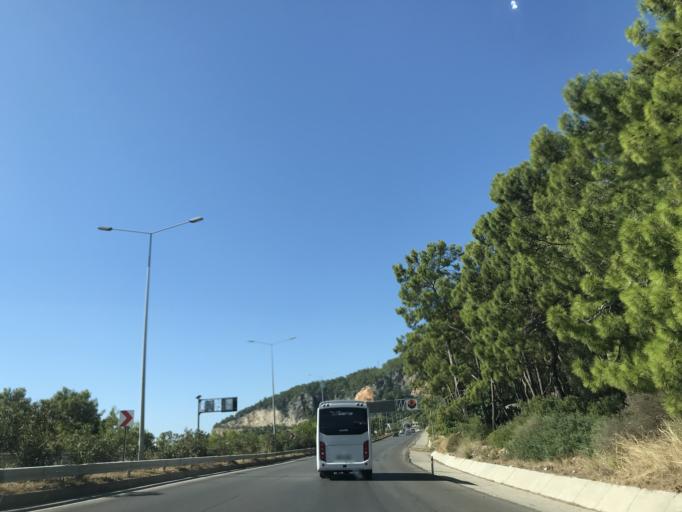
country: TR
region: Antalya
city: Cakirlar
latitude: 36.7584
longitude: 30.5695
